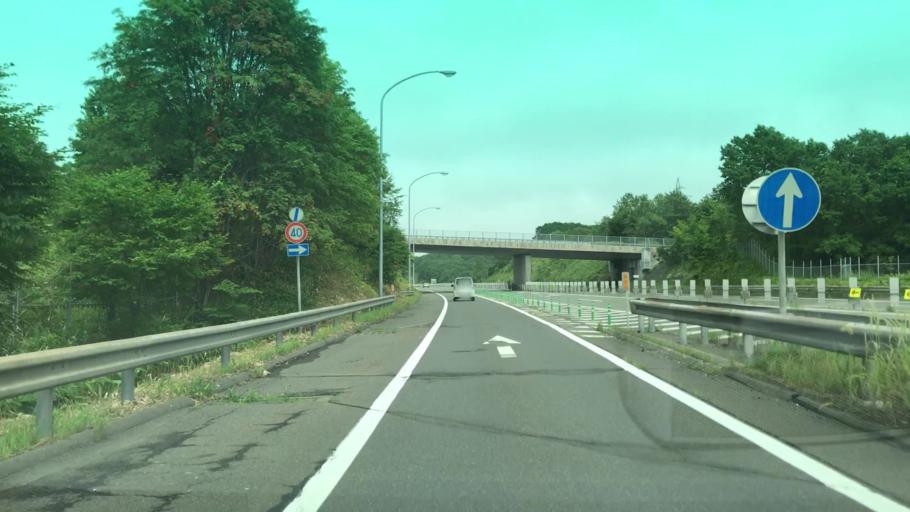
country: JP
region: Hokkaido
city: Tomakomai
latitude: 42.6159
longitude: 141.4707
